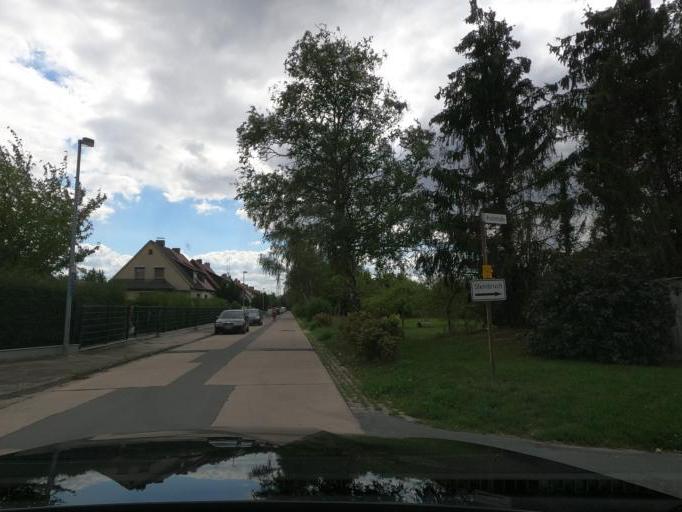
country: DE
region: Lower Saxony
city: Sehnde
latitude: 52.3482
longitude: 9.8902
